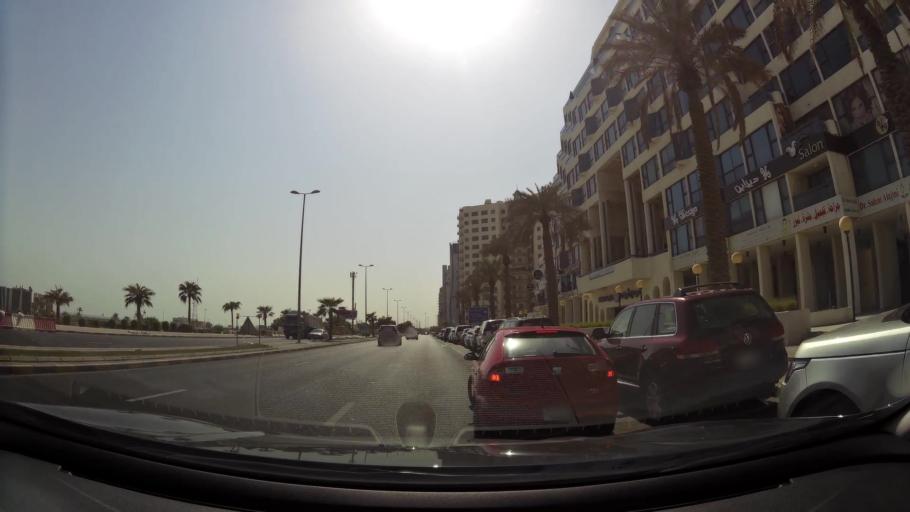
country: KW
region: Muhafazat Hawalli
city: As Salimiyah
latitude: 29.3296
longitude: 48.0914
